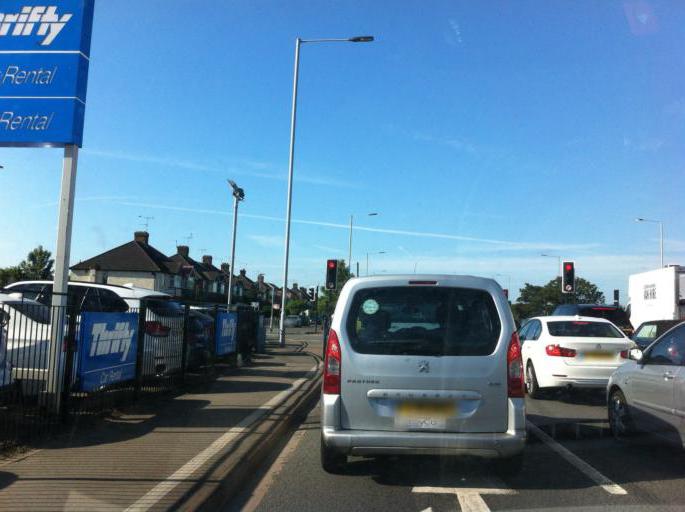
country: GB
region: England
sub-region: Greater London
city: Feltham
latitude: 51.4535
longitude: -0.4438
